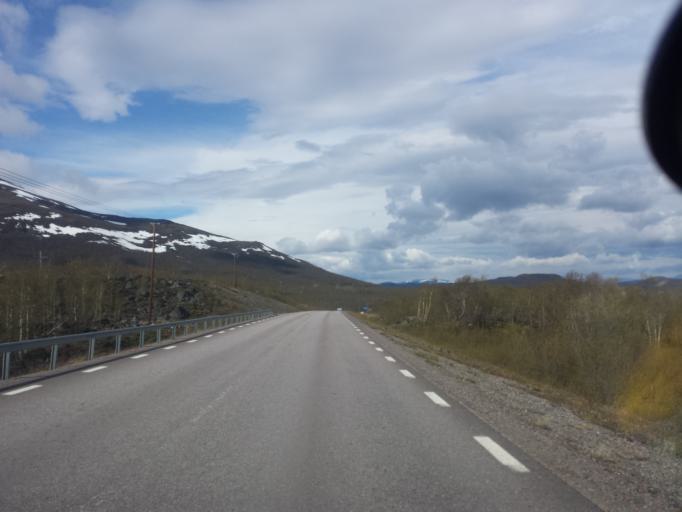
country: SE
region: Norrbotten
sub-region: Kiruna Kommun
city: Kiruna
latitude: 68.1565
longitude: 19.7770
